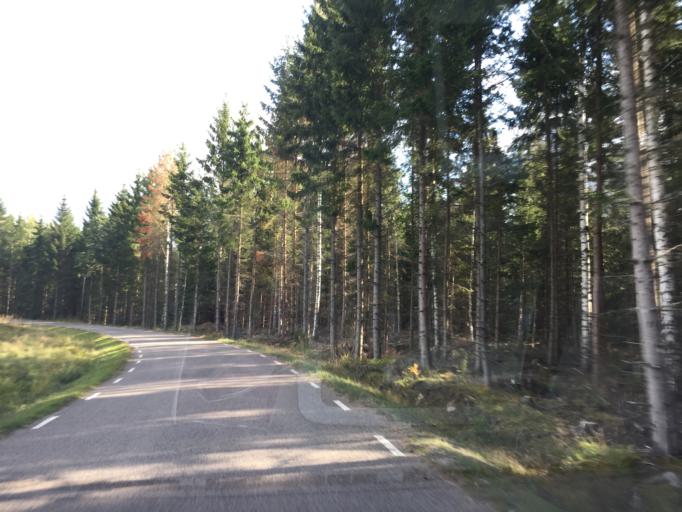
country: SE
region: Soedermanland
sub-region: Vingakers Kommun
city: Vingaker
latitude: 59.0103
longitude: 15.7080
